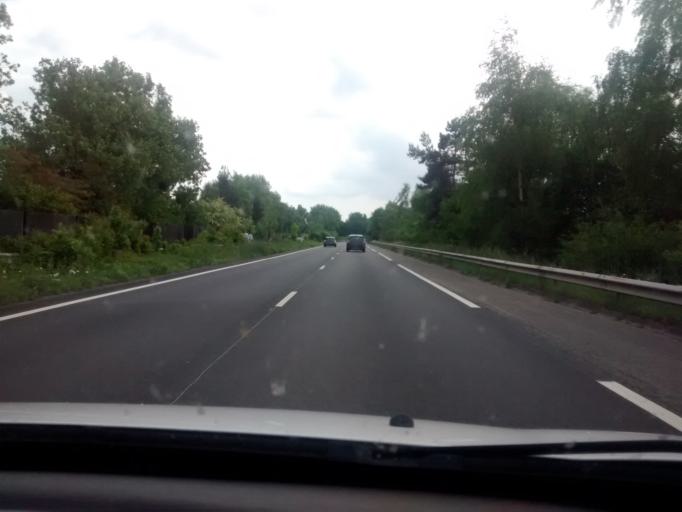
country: FR
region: Ile-de-France
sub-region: Departement des Yvelines
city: Le Perray-en-Yvelines
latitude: 48.6928
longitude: 1.8445
